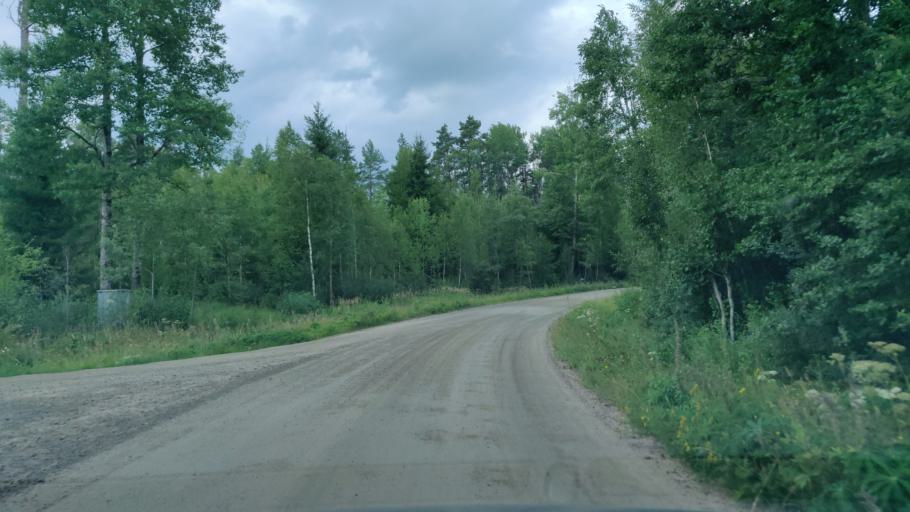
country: SE
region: Vaermland
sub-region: Munkfors Kommun
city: Munkfors
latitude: 59.9599
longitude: 13.4928
